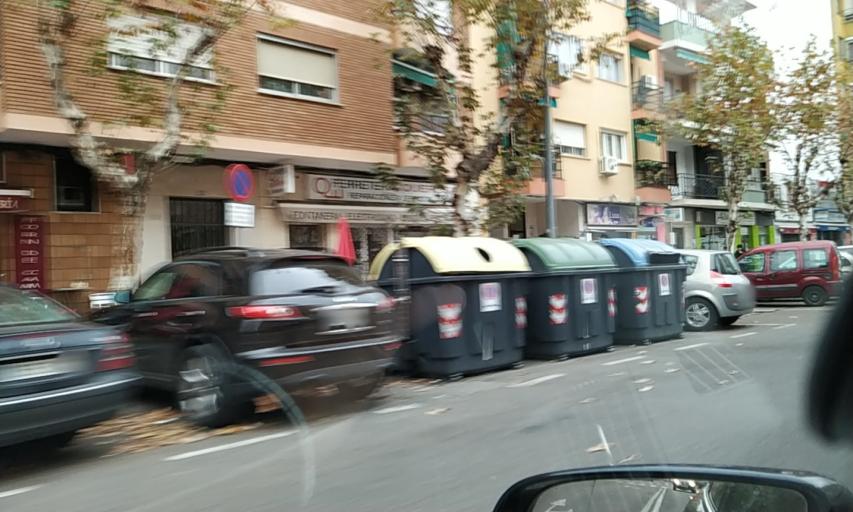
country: ES
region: Extremadura
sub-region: Provincia de Badajoz
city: Badajoz
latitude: 38.8792
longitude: -6.9586
